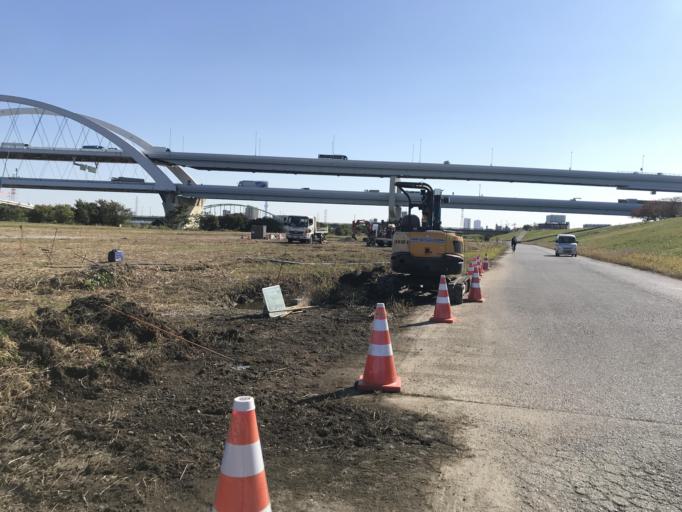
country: JP
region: Saitama
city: Kawaguchi
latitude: 35.7665
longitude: 139.7575
